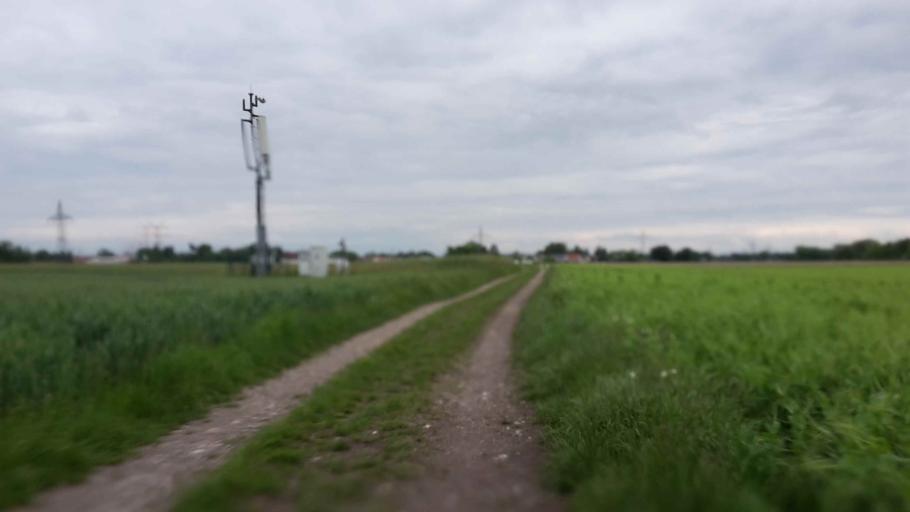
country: DE
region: Bavaria
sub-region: Upper Bavaria
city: Grobenzell
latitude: 48.1895
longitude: 11.4154
